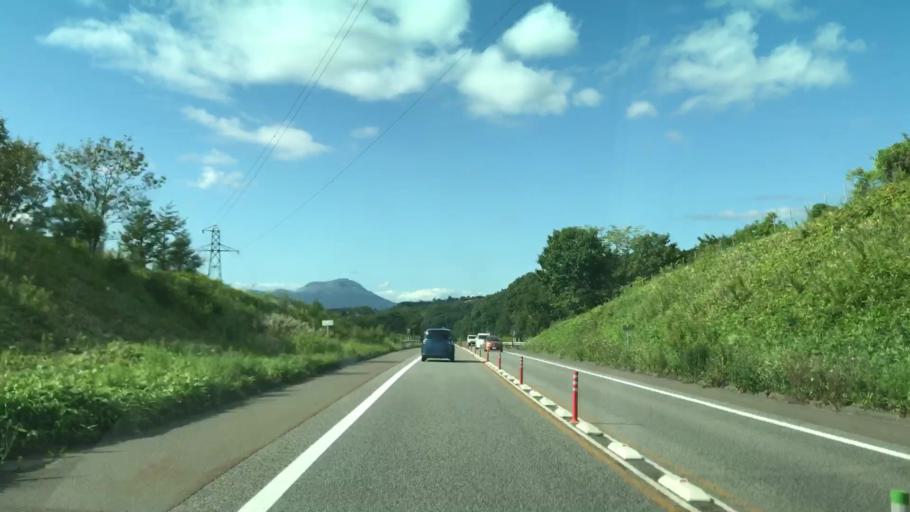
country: JP
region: Hokkaido
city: Date
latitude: 42.4263
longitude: 140.9275
